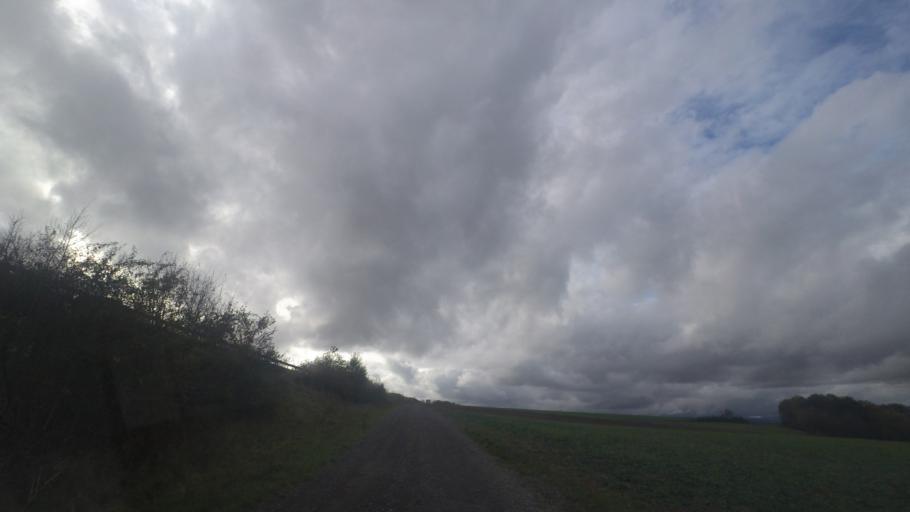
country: DE
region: Bavaria
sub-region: Regierungsbezirk Unterfranken
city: Rodelmaier
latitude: 50.3298
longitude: 10.2792
